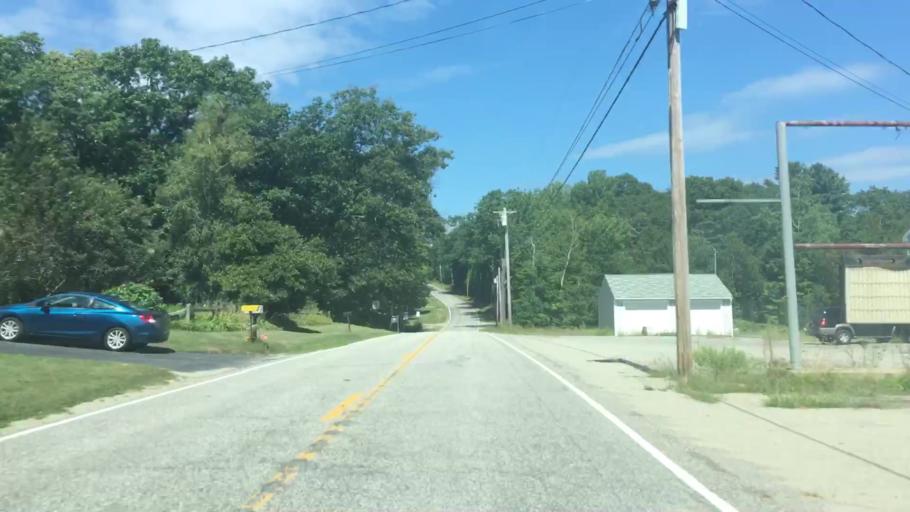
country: US
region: Maine
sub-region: Kennebec County
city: Monmouth
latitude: 44.1629
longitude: -69.9435
